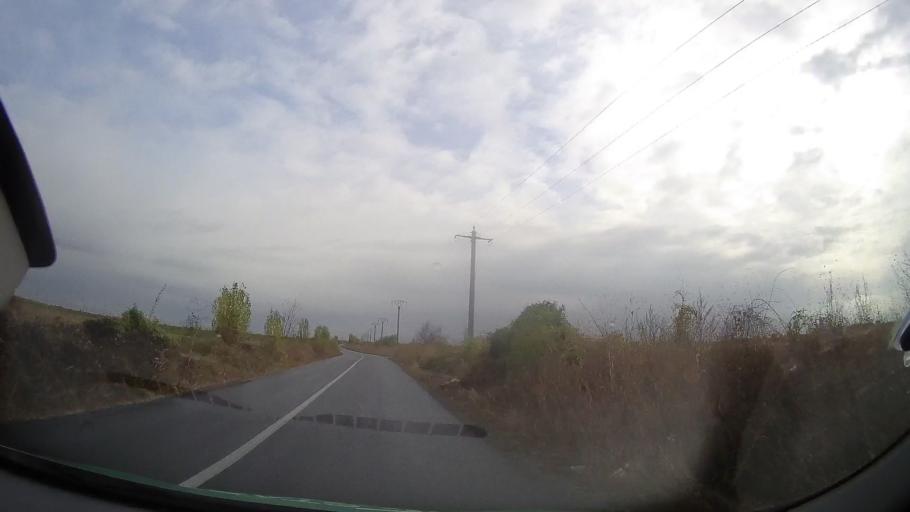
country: RO
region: Ialomita
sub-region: Comuna Maia
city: Maia
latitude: 44.7528
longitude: 26.3867
